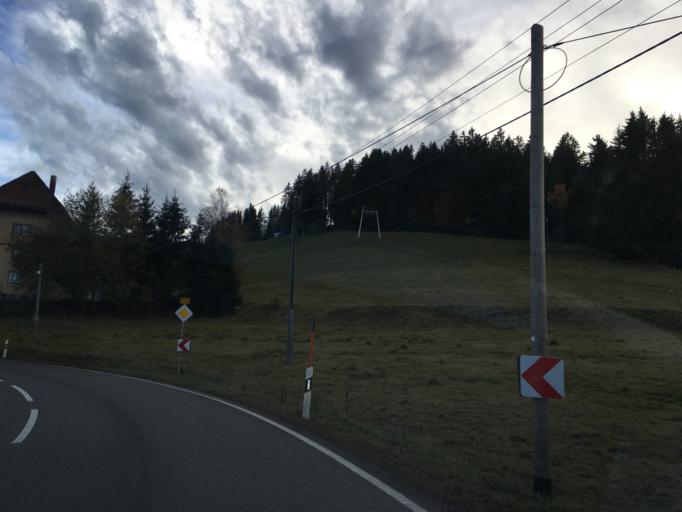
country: DE
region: Baden-Wuerttemberg
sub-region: Freiburg Region
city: Furtwangen im Schwarzwald
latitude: 48.0439
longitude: 8.1863
